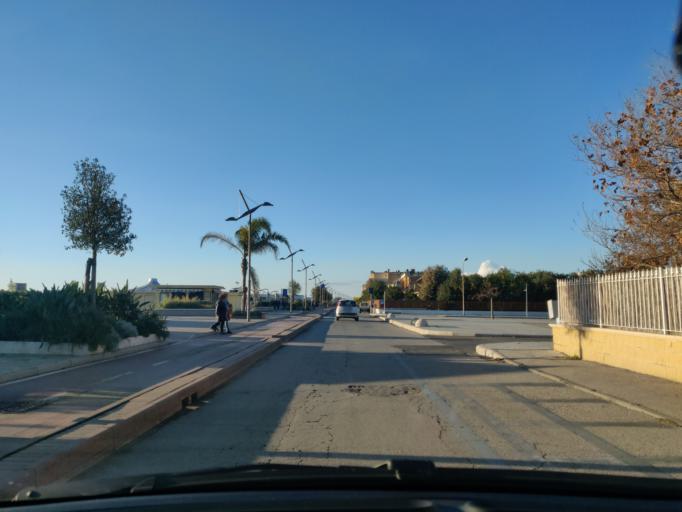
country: IT
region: Latium
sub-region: Provincia di Viterbo
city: Tarquinia
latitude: 42.2196
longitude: 11.7072
